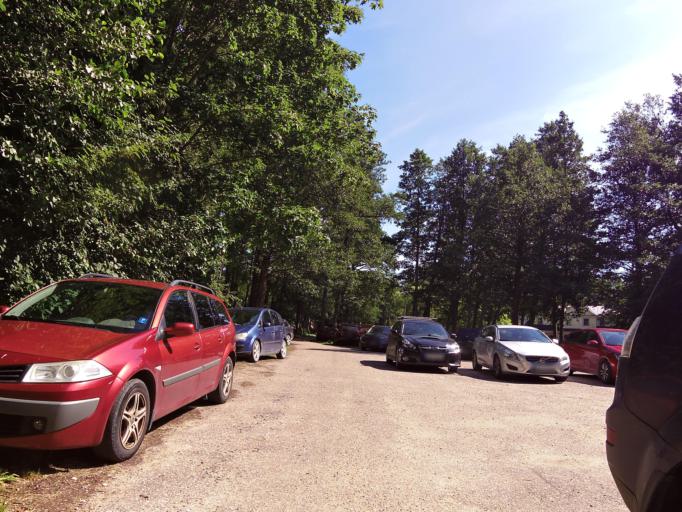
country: EE
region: Hiiumaa
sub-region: Kaerdla linn
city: Kardla
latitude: 58.9326
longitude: 22.3907
